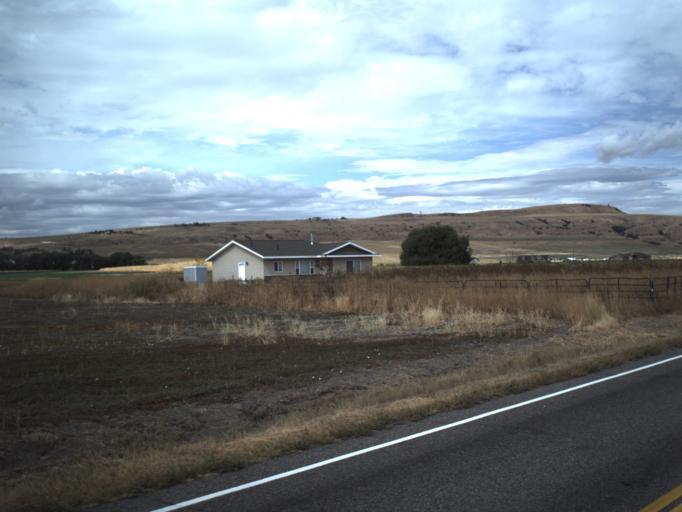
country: US
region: Utah
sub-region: Cache County
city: Mendon
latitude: 41.7640
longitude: -111.9801
